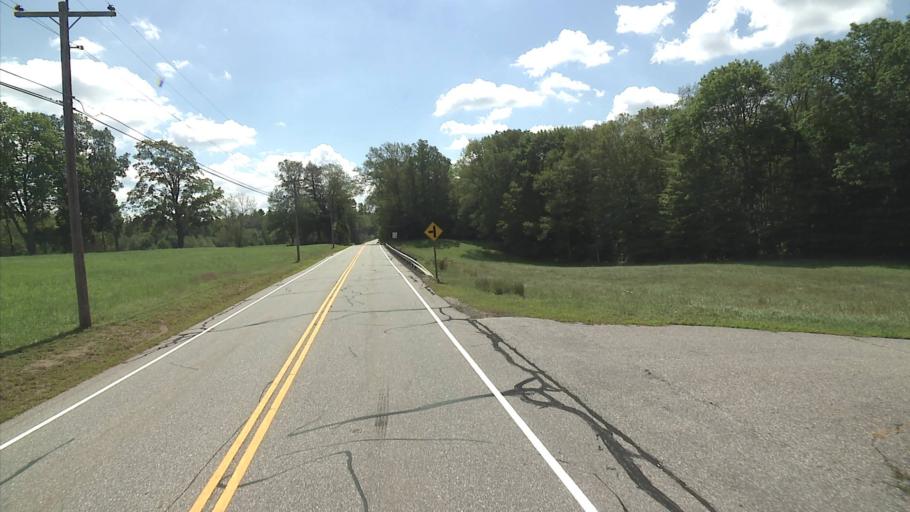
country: US
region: Connecticut
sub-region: Windham County
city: South Woodstock
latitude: 41.9204
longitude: -72.0794
